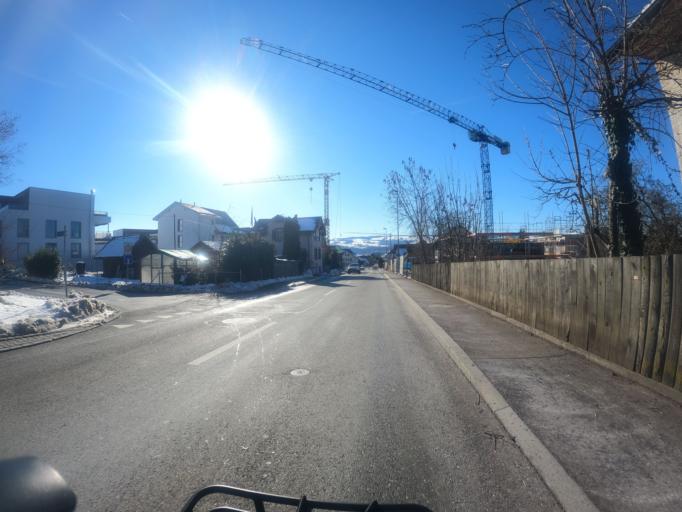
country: CH
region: Zurich
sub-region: Bezirk Affoltern
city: Ottenbach
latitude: 47.2838
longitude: 8.4083
